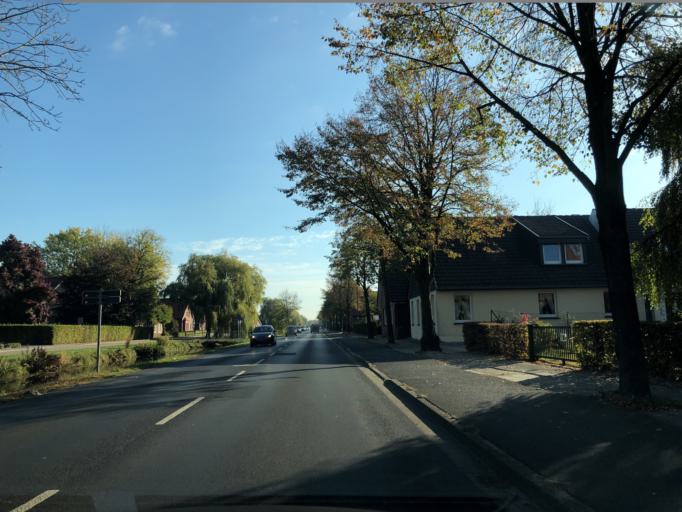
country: DE
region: Lower Saxony
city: Papenburg
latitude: 53.0812
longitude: 7.4205
